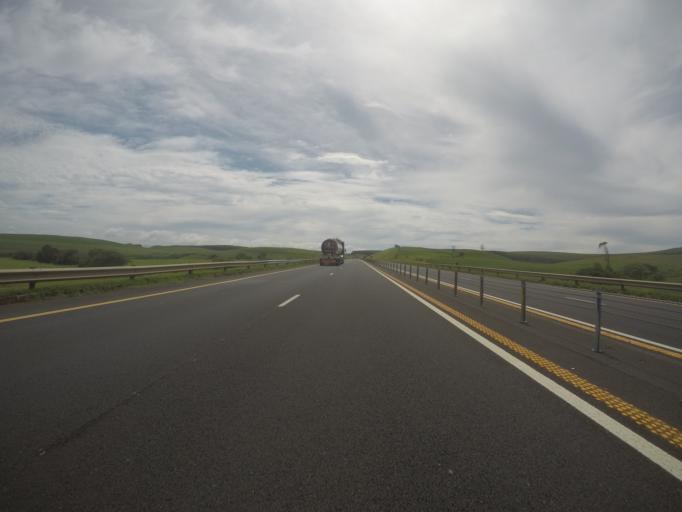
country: ZA
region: KwaZulu-Natal
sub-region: uThungulu District Municipality
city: Eshowe
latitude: -29.0515
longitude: 31.6363
